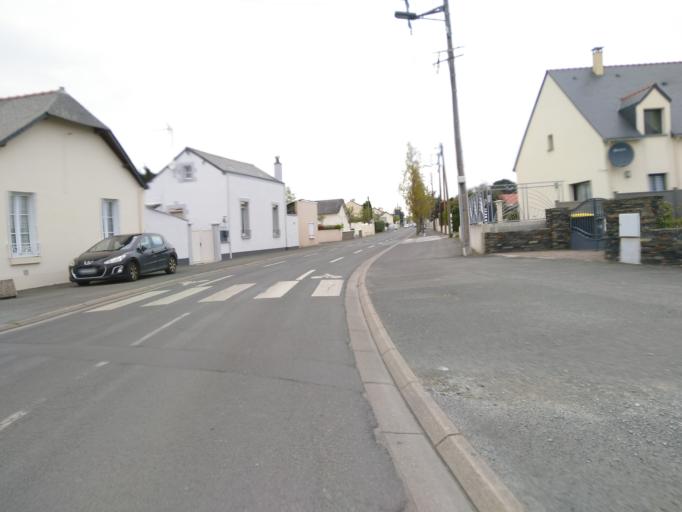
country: FR
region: Pays de la Loire
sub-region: Departement de Maine-et-Loire
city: Les Ponts-de-Ce
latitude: 47.4466
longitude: -0.5181
